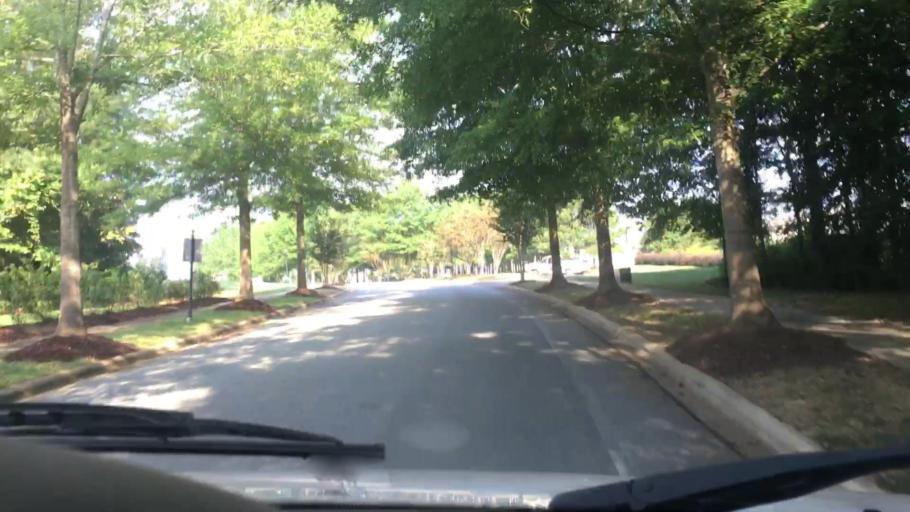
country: US
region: North Carolina
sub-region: Gaston County
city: Davidson
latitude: 35.4777
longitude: -80.8174
